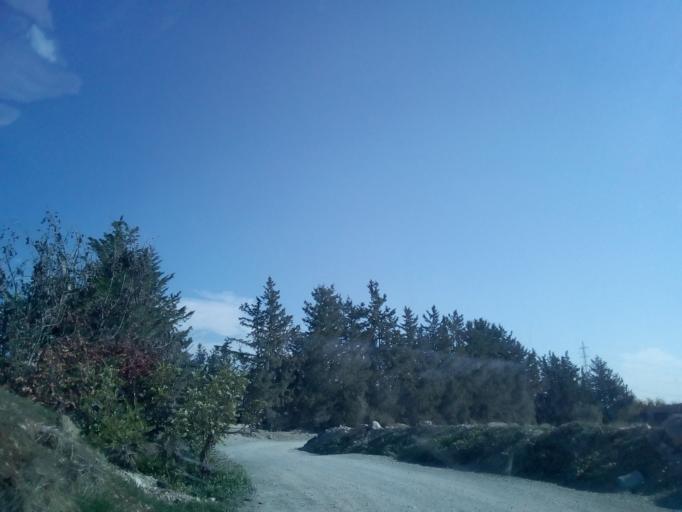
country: CY
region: Limassol
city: Ypsonas
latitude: 34.6771
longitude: 32.9793
